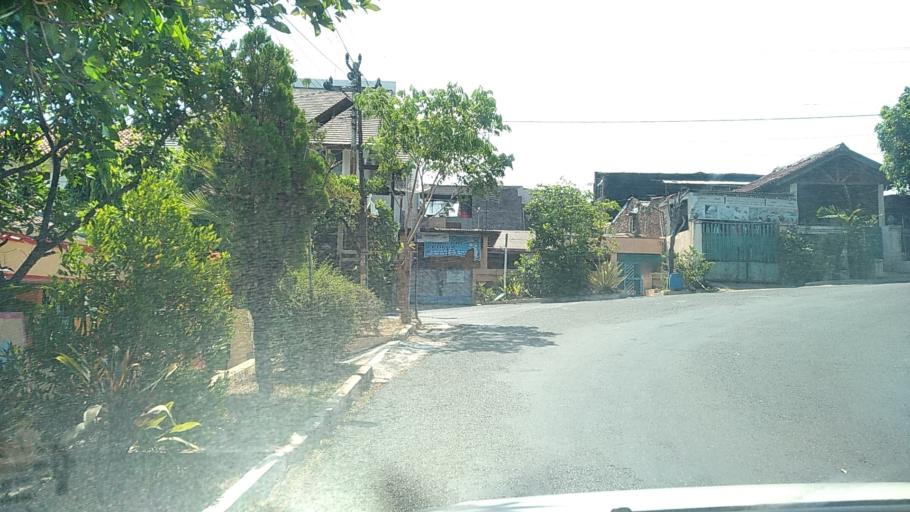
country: ID
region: Central Java
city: Ungaran
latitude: -7.0735
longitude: 110.4275
